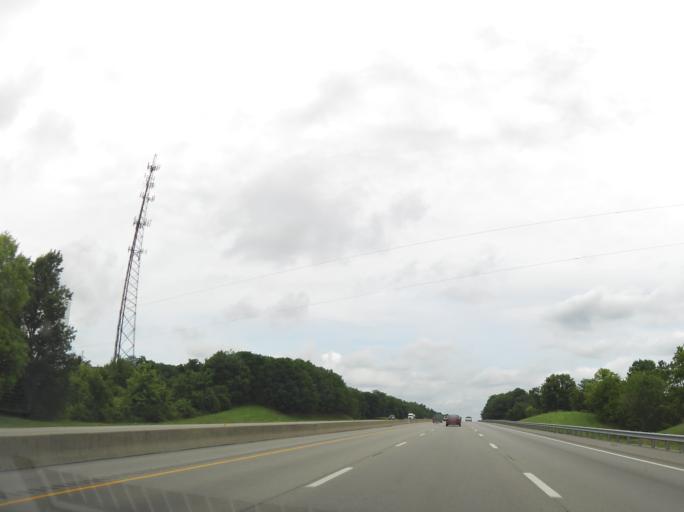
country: US
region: Kentucky
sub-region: Scott County
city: Georgetown
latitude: 38.3086
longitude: -84.5588
